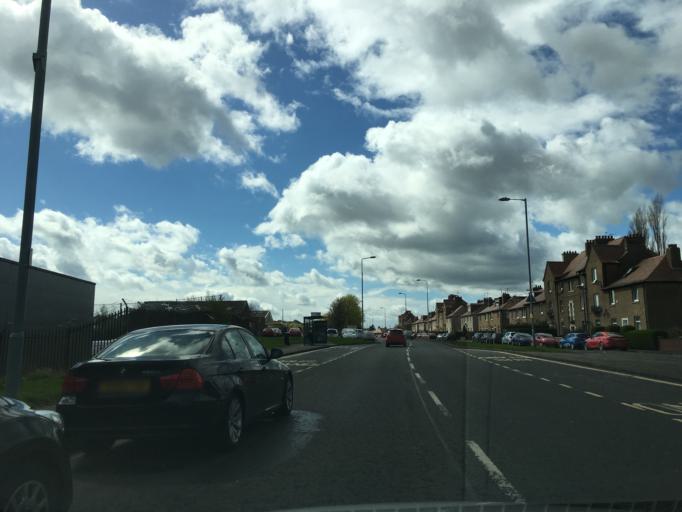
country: GB
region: Scotland
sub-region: Edinburgh
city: Colinton
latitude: 55.9247
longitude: -3.2671
